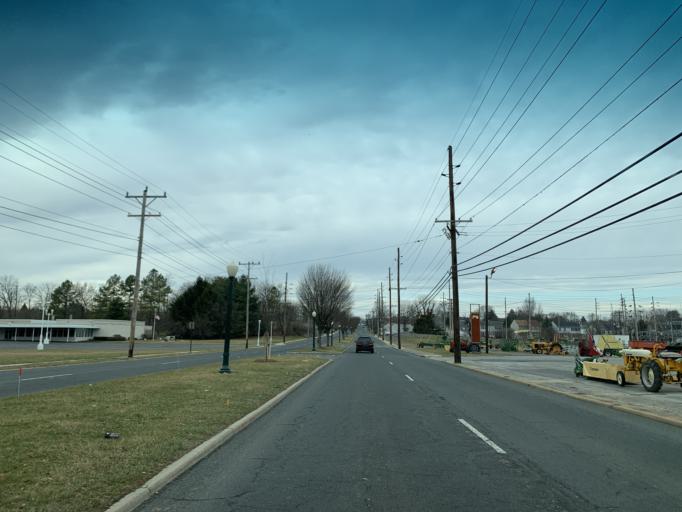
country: US
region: Maryland
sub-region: Washington County
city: Hagerstown
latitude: 39.6223
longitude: -77.7188
